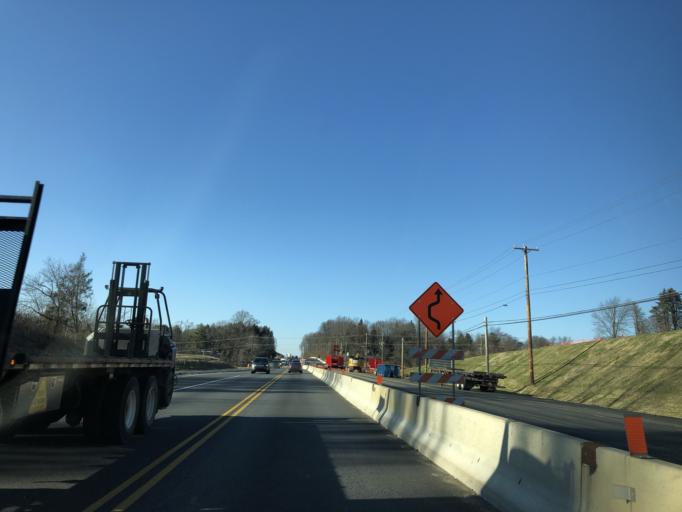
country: US
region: Pennsylvania
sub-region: Delaware County
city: Chester Heights
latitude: 39.8709
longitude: -75.4999
